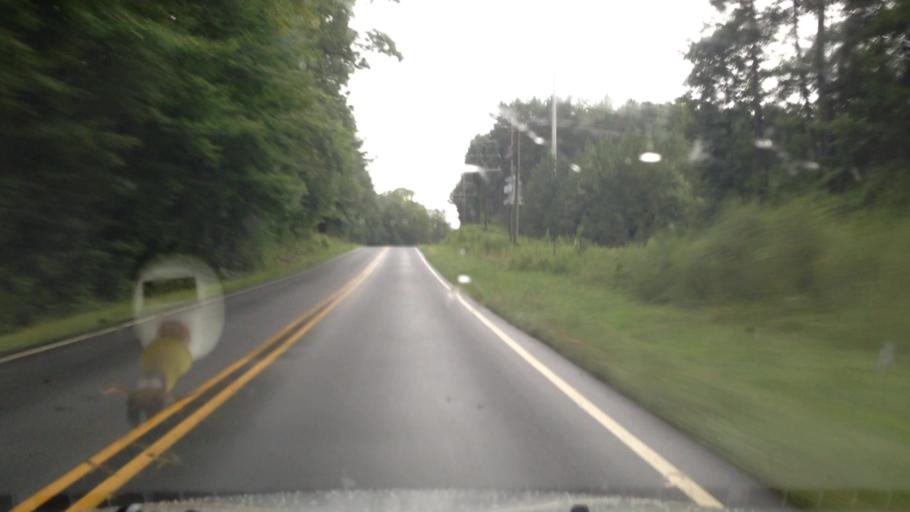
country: US
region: North Carolina
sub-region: Rockingham County
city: Reidsville
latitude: 36.2630
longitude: -79.7264
